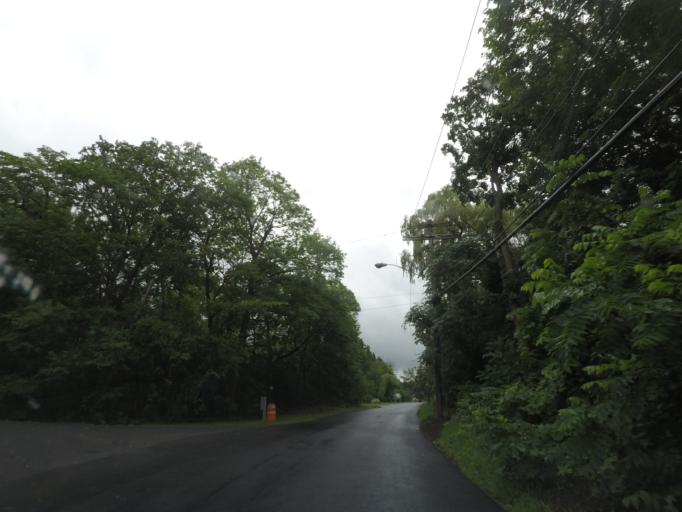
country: US
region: New York
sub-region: Rensselaer County
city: Rensselaer
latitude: 42.6331
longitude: -73.7352
